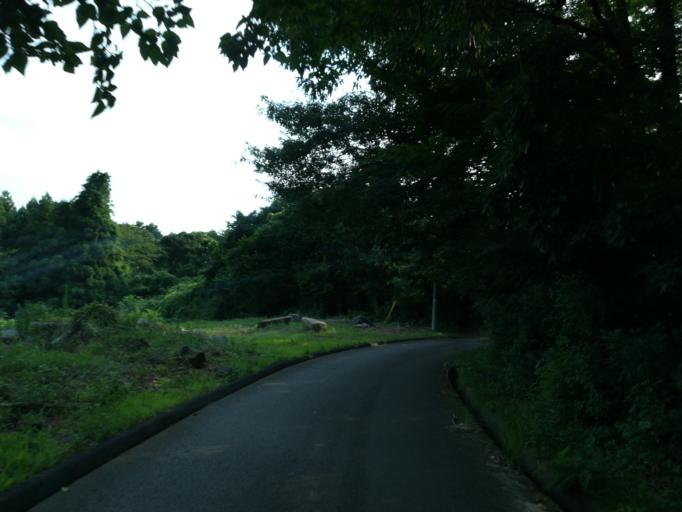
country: JP
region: Ibaraki
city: Tsukuba
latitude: 36.2049
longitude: 140.1126
